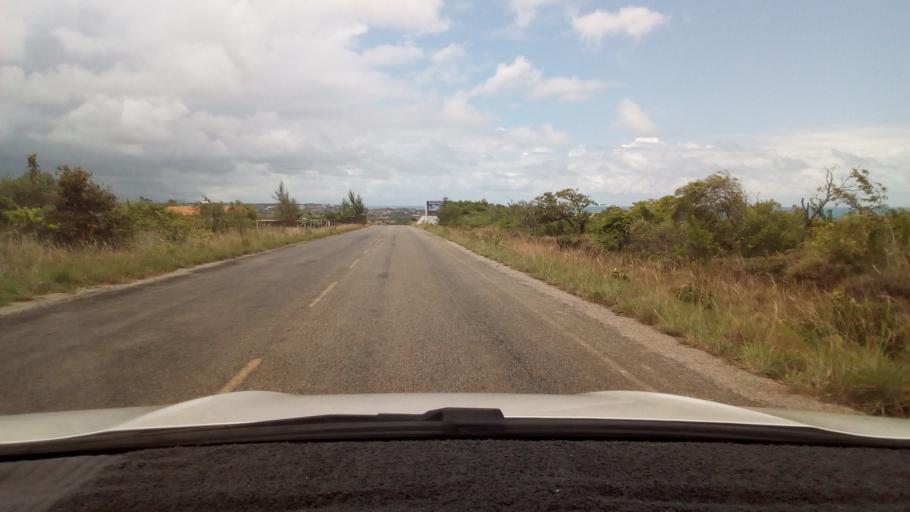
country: BR
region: Paraiba
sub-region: Conde
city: Conde
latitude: -7.3247
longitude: -34.8083
